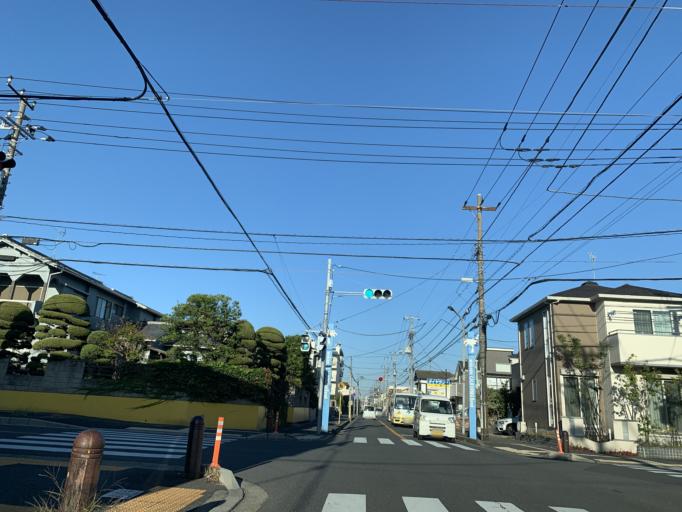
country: JP
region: Tokyo
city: Urayasu
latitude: 35.6849
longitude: 139.9214
